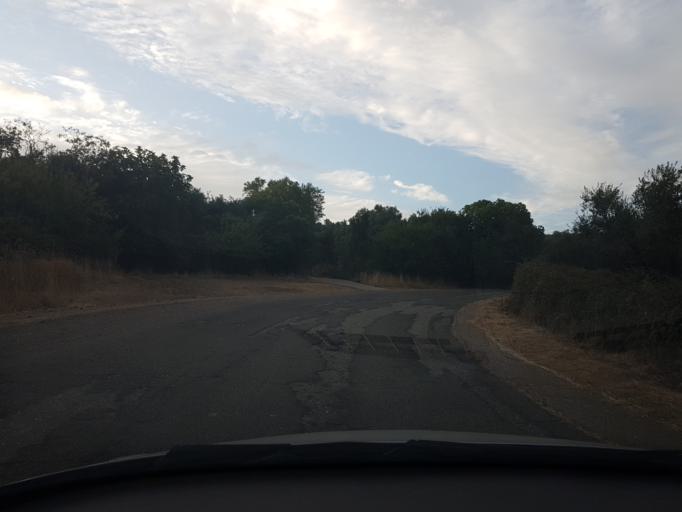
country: IT
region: Sardinia
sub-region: Provincia di Oristano
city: Seneghe
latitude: 40.1062
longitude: 8.6217
